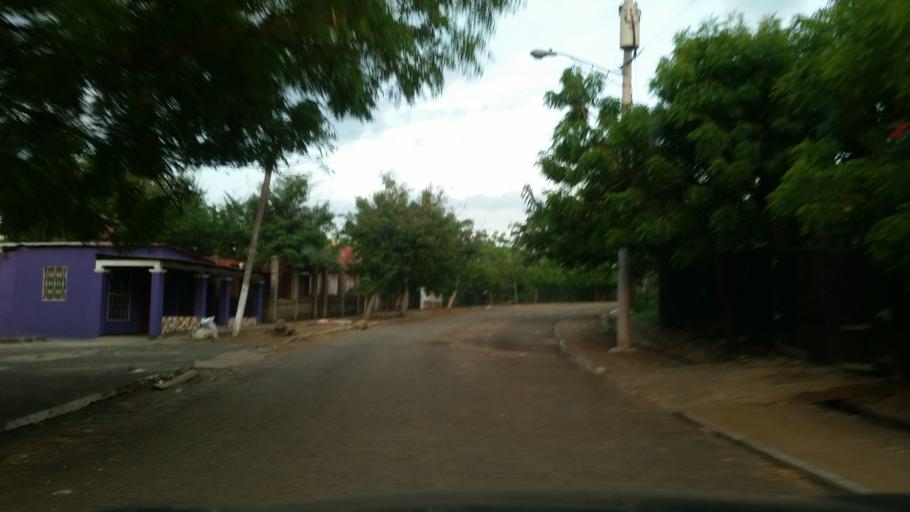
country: NI
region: Managua
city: Masachapa
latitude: 11.7705
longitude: -86.5037
